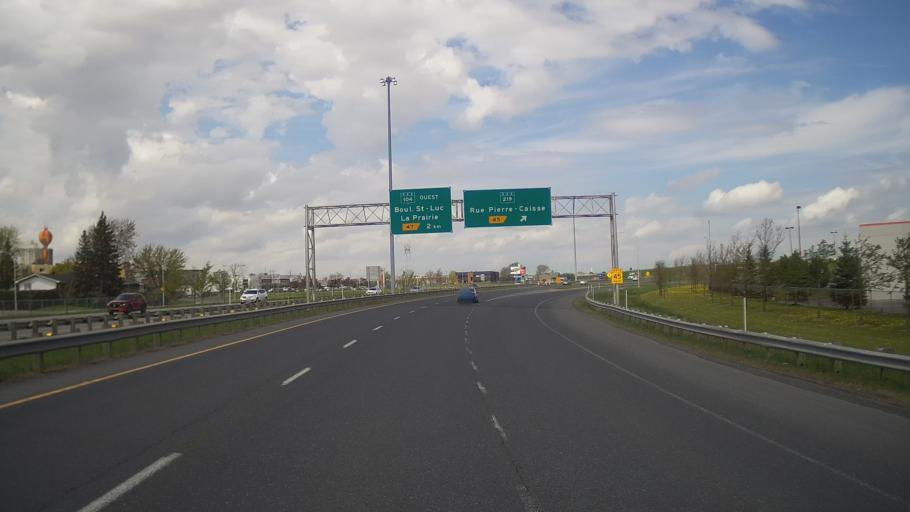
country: CA
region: Quebec
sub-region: Monteregie
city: Saint-Jean-sur-Richelieu
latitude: 45.3275
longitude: -73.2834
